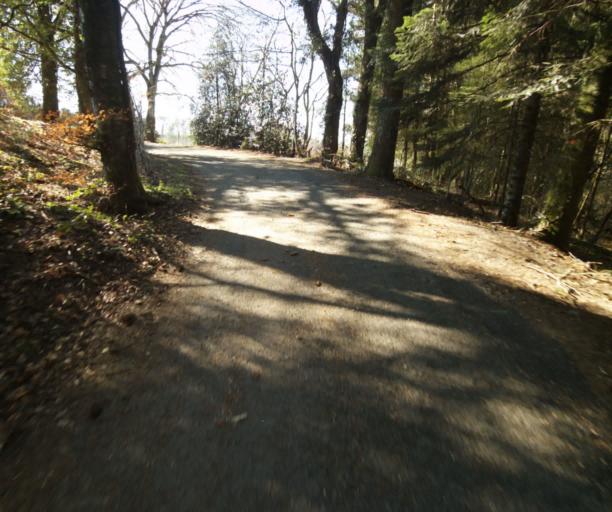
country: FR
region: Limousin
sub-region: Departement de la Correze
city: Chamboulive
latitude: 45.4884
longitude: 1.7436
